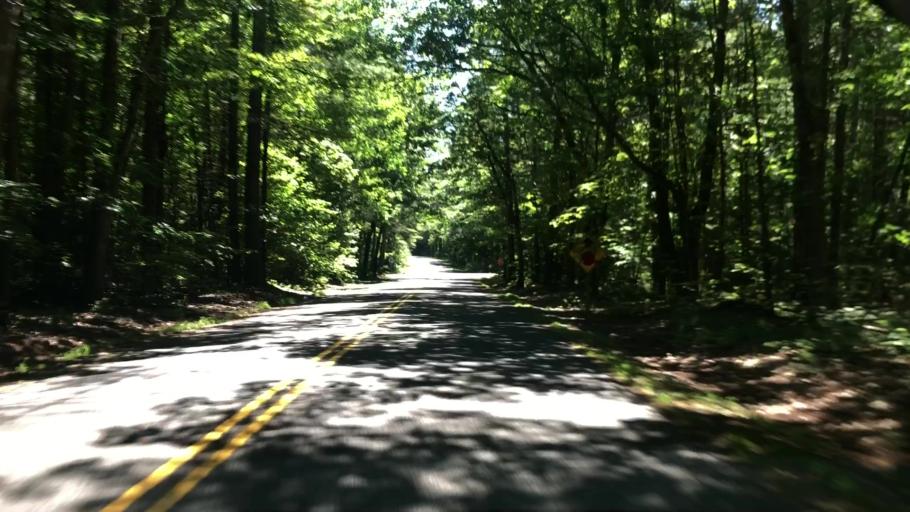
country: US
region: New Hampshire
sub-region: Hillsborough County
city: Milford
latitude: 42.8400
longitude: -71.5719
